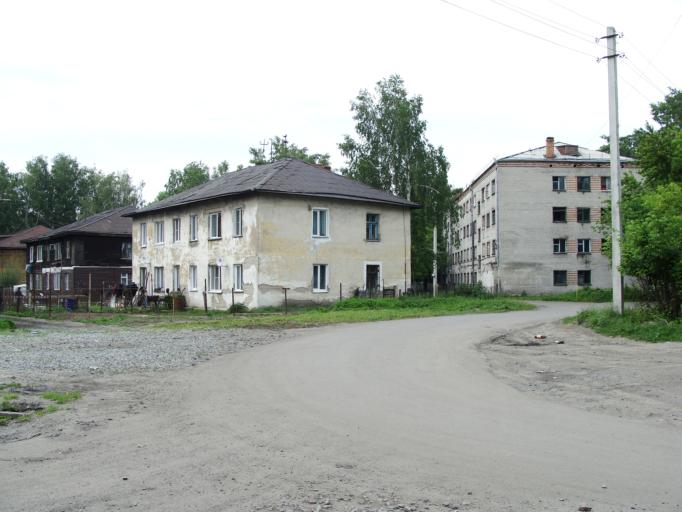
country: RU
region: Altai Krai
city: Yuzhnyy
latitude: 53.2821
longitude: 83.7463
